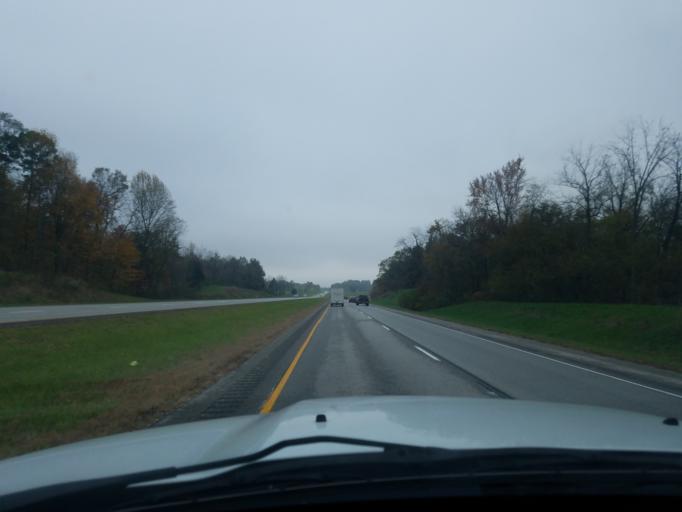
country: US
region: Kentucky
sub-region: Larue County
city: Hodgenville
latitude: 37.6210
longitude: -85.8119
